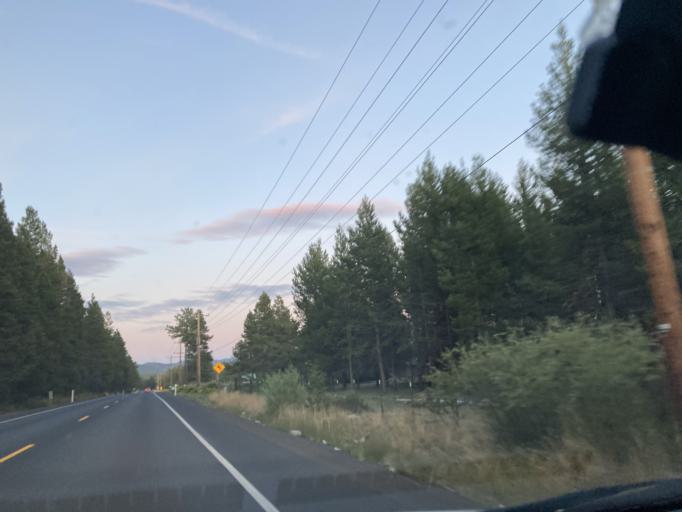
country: US
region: Oregon
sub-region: Deschutes County
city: Three Rivers
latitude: 43.8195
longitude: -121.4608
